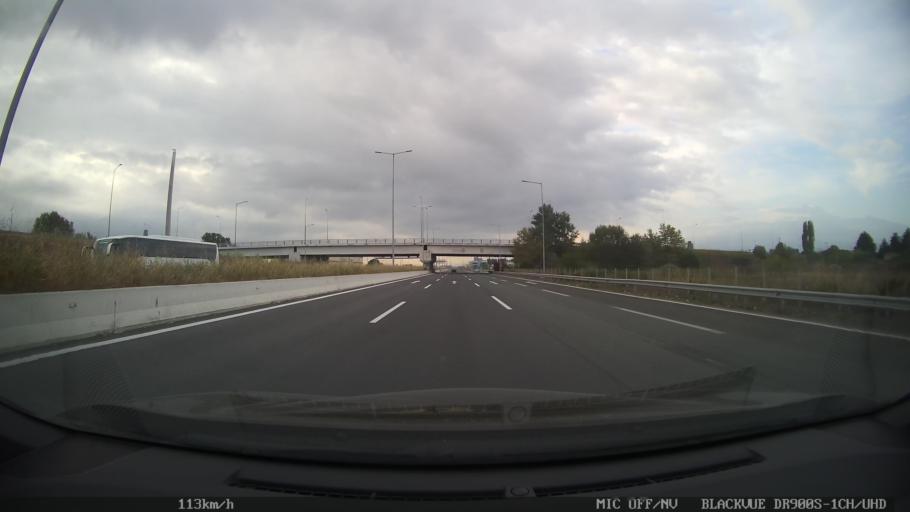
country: GR
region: Central Macedonia
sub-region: Nomos Pierias
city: Peristasi
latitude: 40.2567
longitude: 22.5313
